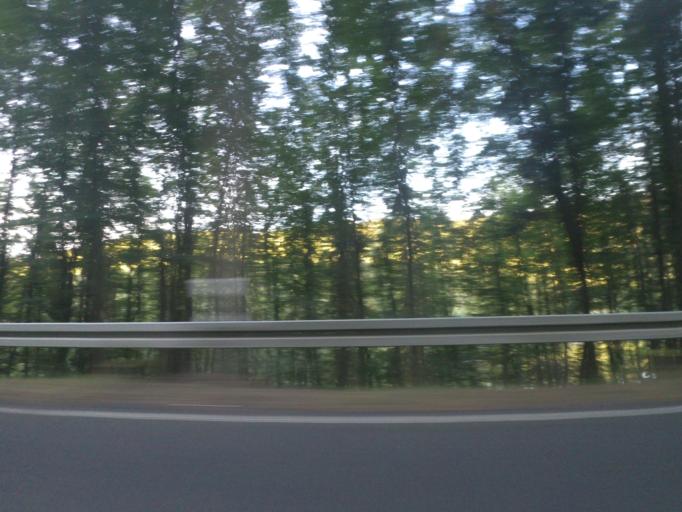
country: DE
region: Hesse
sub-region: Regierungsbezirk Darmstadt
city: Gelnhausen
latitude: 50.2660
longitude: 9.2162
